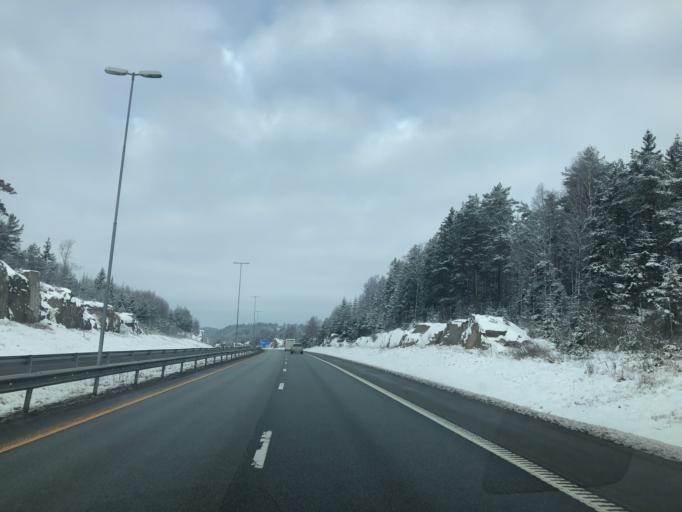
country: NO
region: Ostfold
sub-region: Sarpsborg
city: Skjeberg
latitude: 59.1702
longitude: 11.2158
